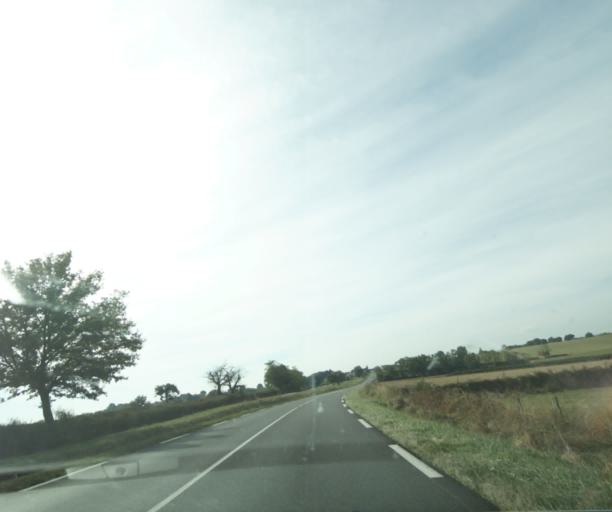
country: FR
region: Auvergne
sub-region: Departement de l'Allier
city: Saint-Francois
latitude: 46.4290
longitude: 3.9096
